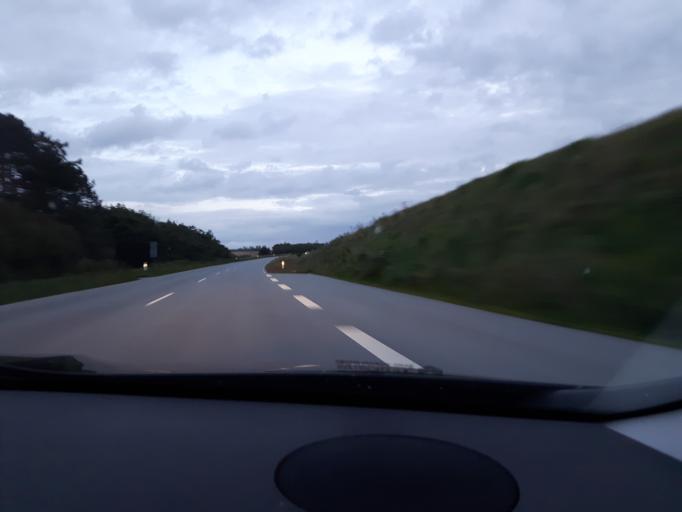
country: DK
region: North Denmark
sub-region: Hjorring Kommune
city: Hjorring
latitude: 57.5115
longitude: 9.9486
